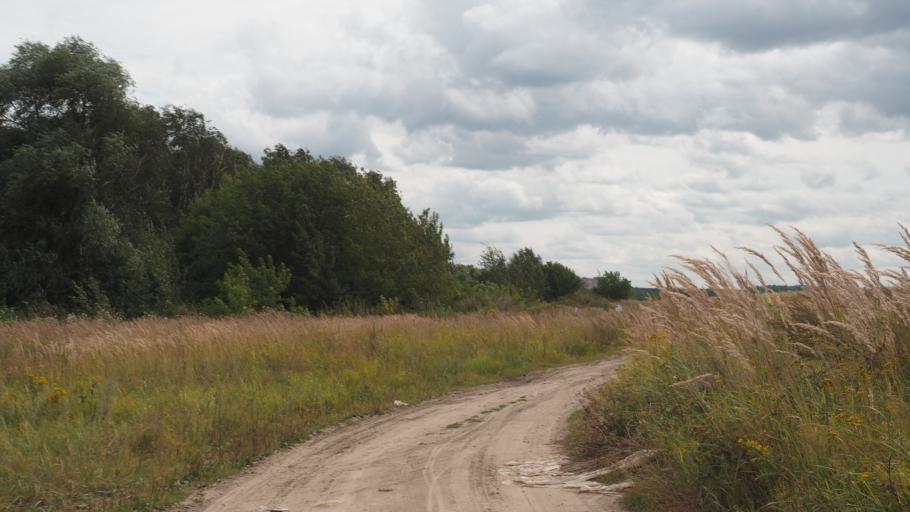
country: RU
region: Moskovskaya
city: Ramenskoye
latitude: 55.5633
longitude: 38.2880
